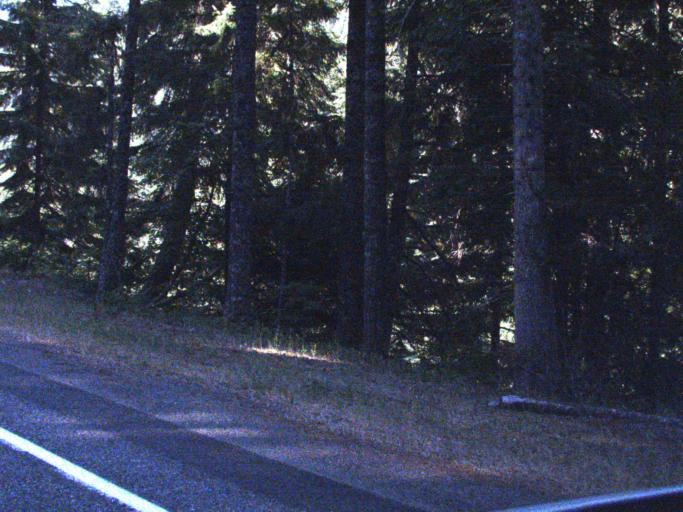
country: US
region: Washington
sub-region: King County
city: Enumclaw
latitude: 47.0457
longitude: -121.5700
